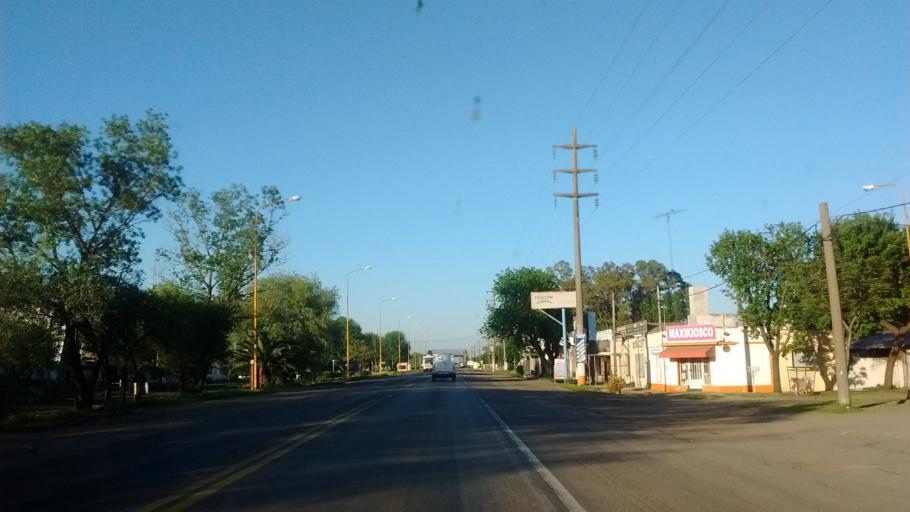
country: AR
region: Santa Fe
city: Firmat
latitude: -33.4506
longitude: -61.4926
